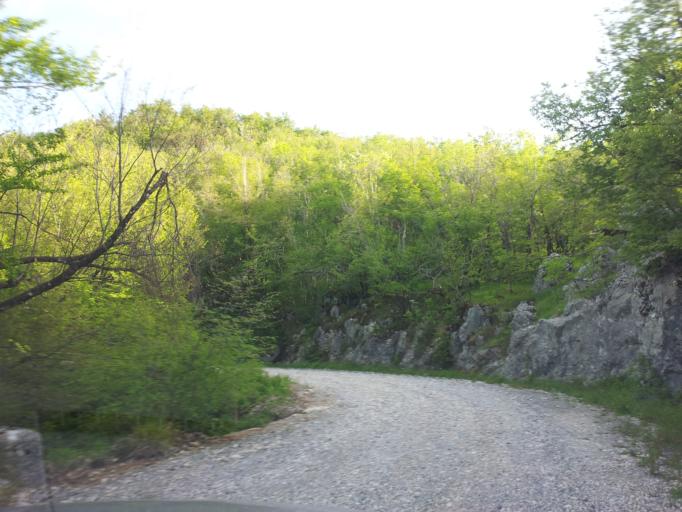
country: HR
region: Zadarska
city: Obrovac
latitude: 44.3035
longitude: 15.6604
